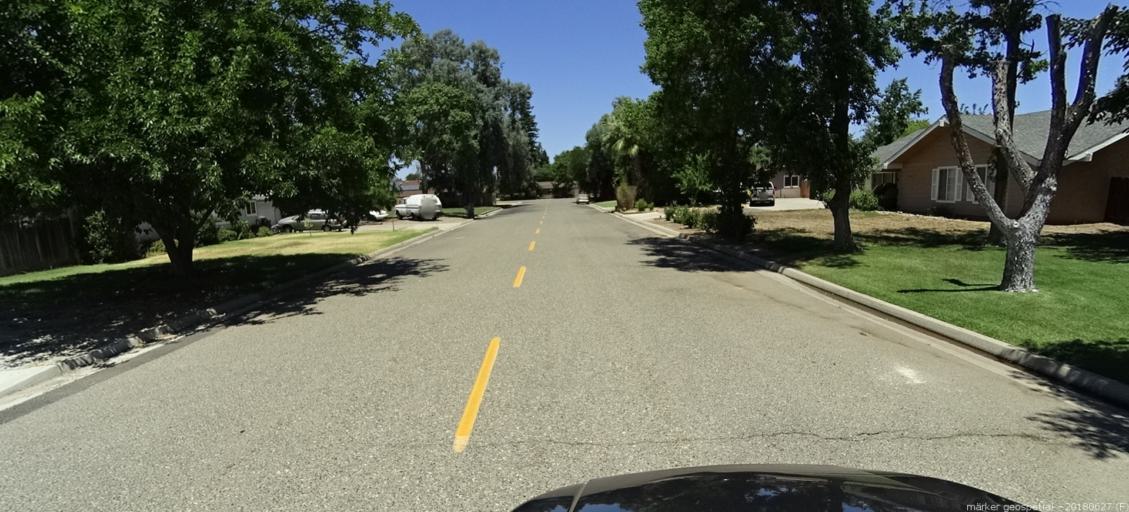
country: US
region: California
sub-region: Madera County
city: Bonadelle Ranchos-Madera Ranchos
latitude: 36.9273
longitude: -119.8927
